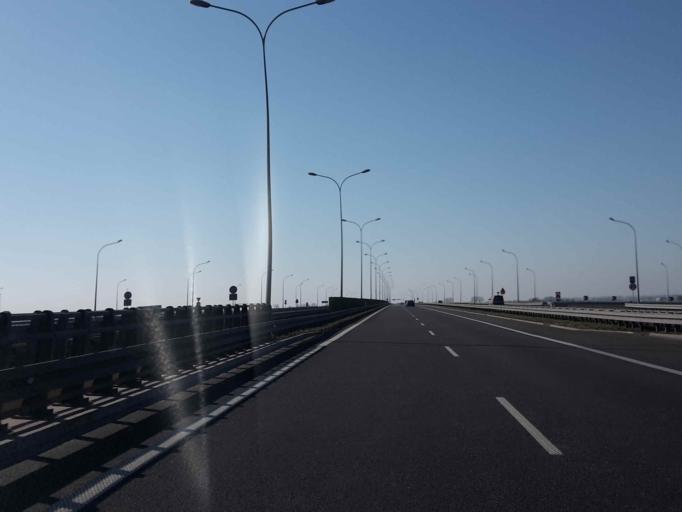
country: PL
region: Greater Poland Voivodeship
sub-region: Powiat poznanski
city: Kostrzyn
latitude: 52.3969
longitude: 17.2571
